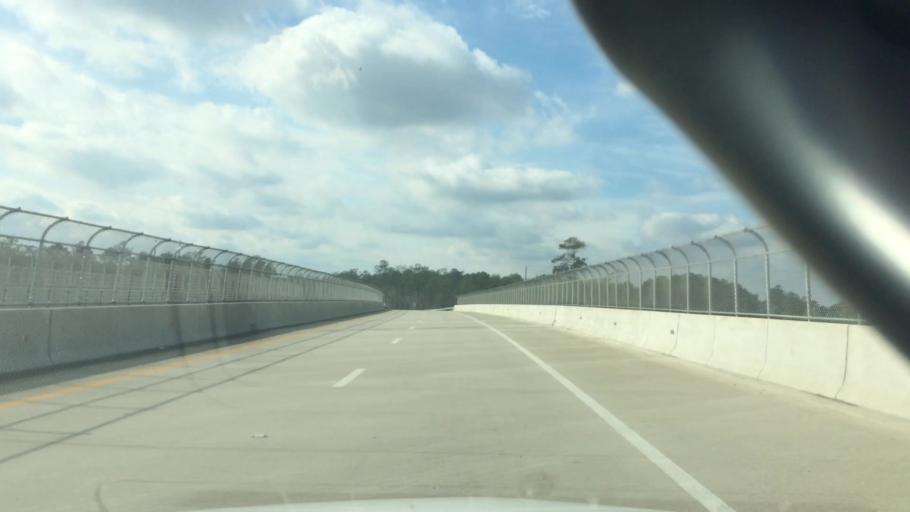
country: US
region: North Carolina
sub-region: Brunswick County
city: Leland
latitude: 34.2798
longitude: -78.0600
